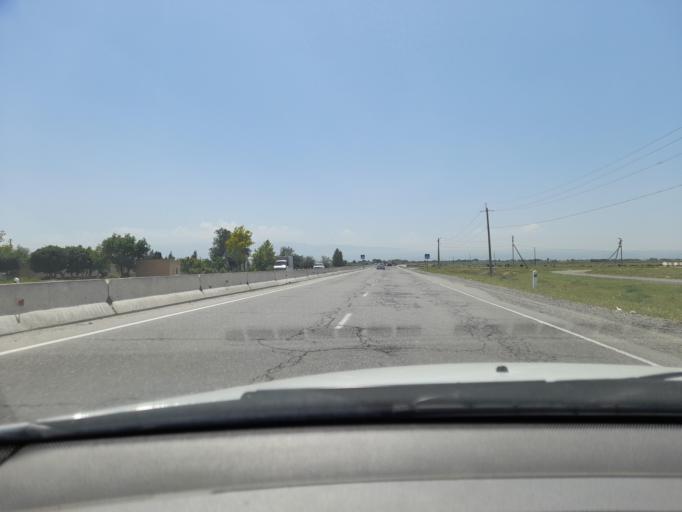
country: UZ
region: Jizzax
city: Jizzax
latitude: 40.1767
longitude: 67.9657
